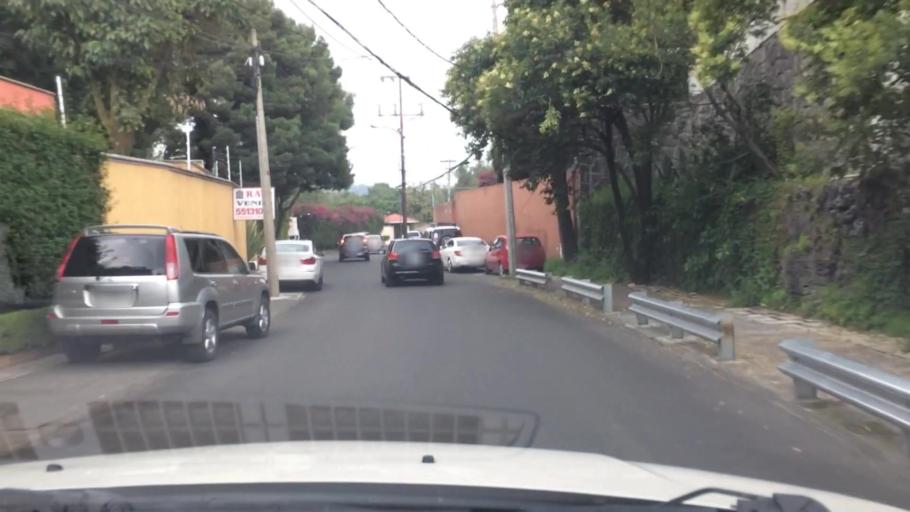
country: MX
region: Mexico City
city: Magdalena Contreras
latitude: 19.3161
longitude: -99.2102
